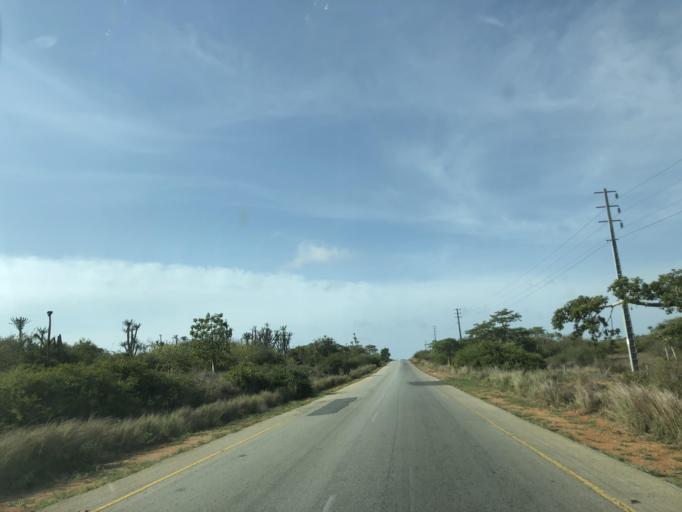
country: AO
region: Luanda
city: Luanda
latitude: -9.2948
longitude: 13.1342
